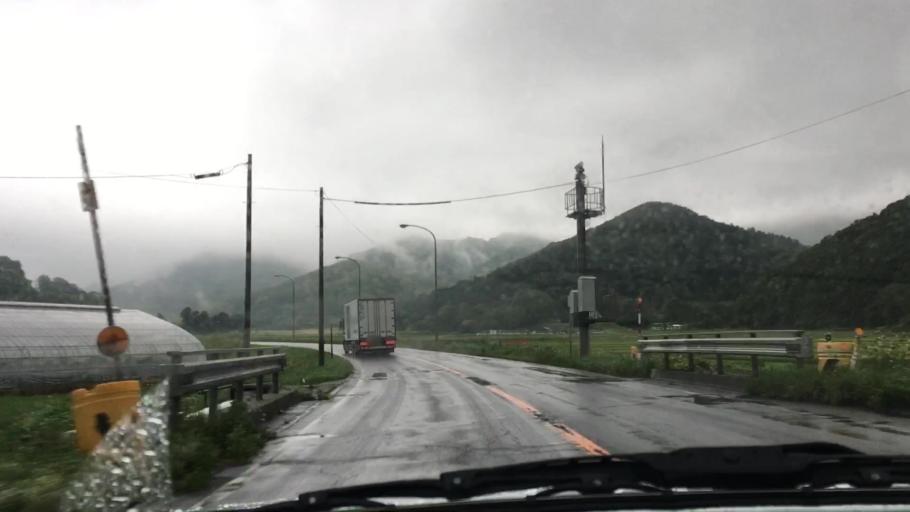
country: JP
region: Hokkaido
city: Niseko Town
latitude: 42.6004
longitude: 140.5877
